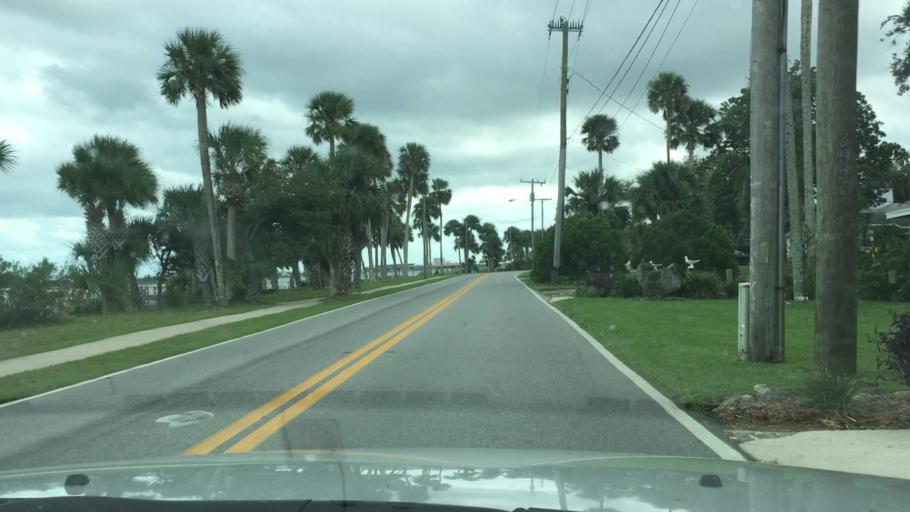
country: US
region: Florida
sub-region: Volusia County
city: Ormond Beach
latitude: 29.2766
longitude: -81.0508
